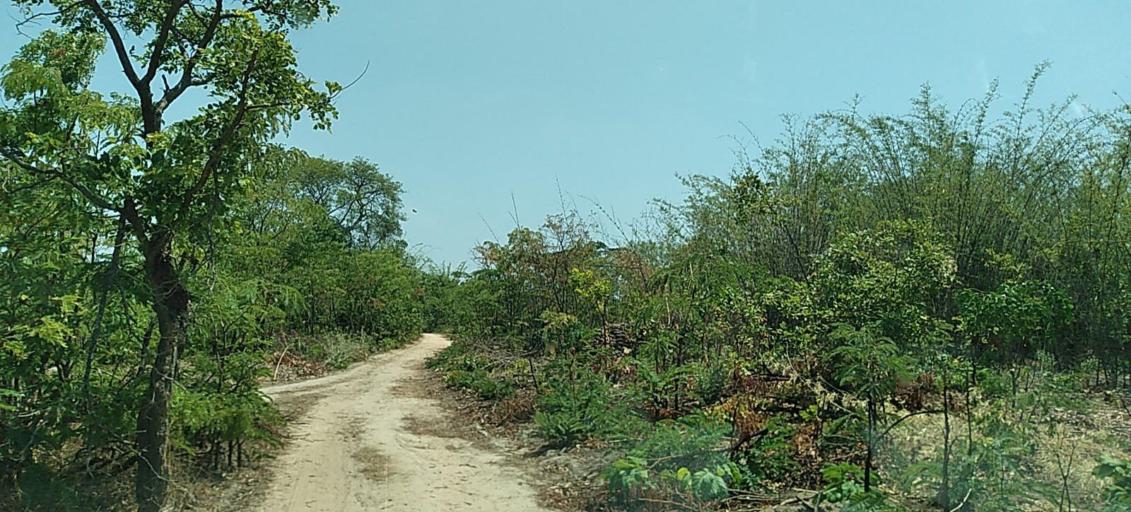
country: ZM
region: Copperbelt
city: Luanshya
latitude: -12.9918
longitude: 28.3280
